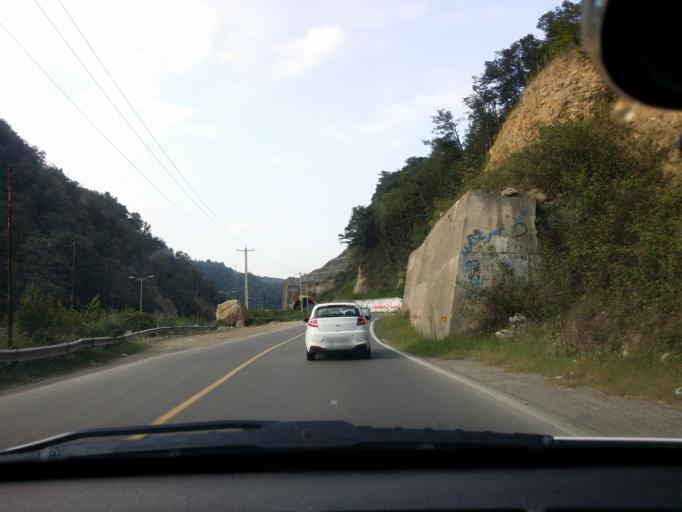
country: IR
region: Mazandaran
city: Chalus
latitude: 36.5726
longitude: 51.3809
